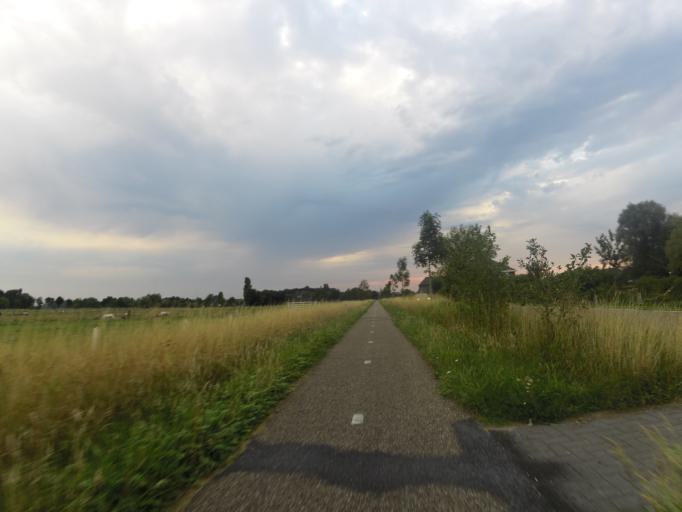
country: NL
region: Gelderland
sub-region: Oude IJsselstreek
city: Gendringen
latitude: 51.9115
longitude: 6.3501
